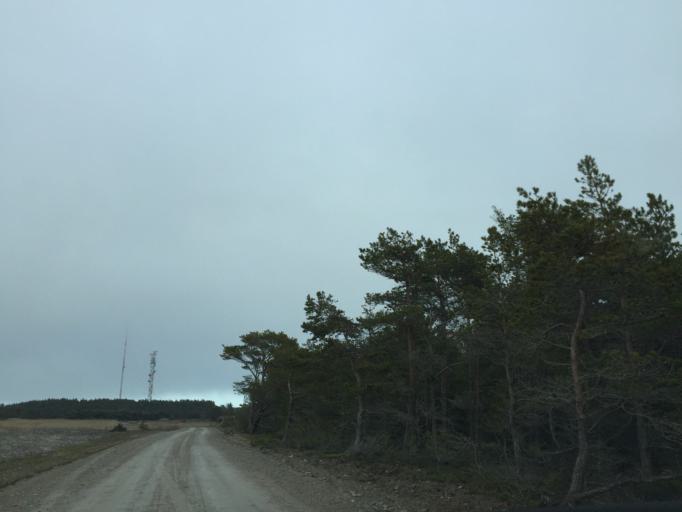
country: EE
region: Saare
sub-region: Kuressaare linn
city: Kuressaare
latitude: 58.5099
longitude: 21.9153
